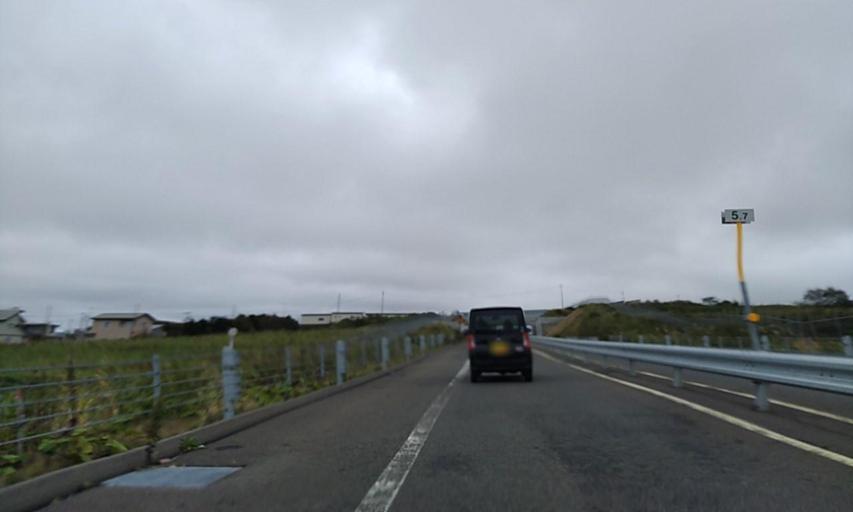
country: JP
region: Hokkaido
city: Nemuro
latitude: 43.3113
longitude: 145.5440
